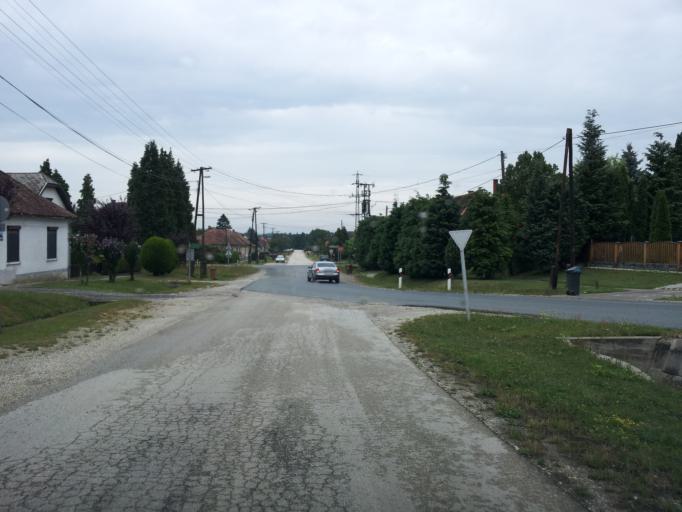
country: HU
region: Vas
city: Kormend
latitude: 46.9656
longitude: 16.6121
